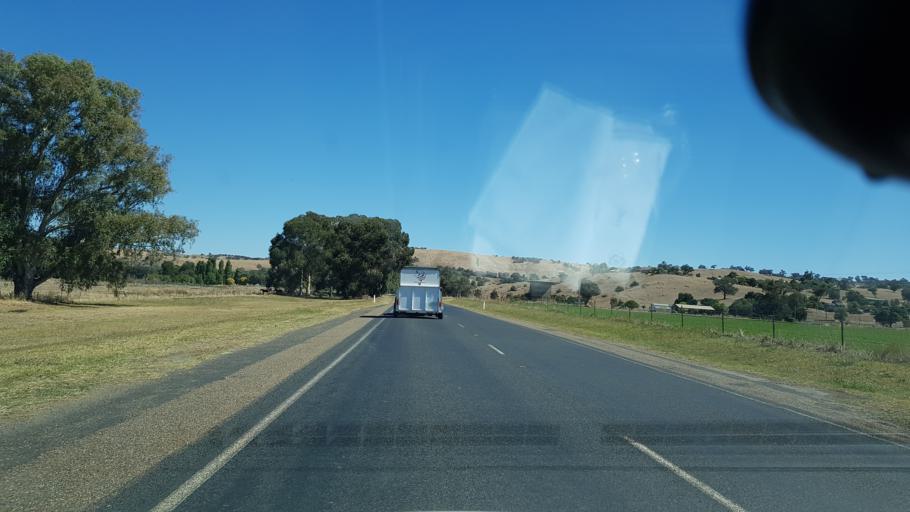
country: AU
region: New South Wales
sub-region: Gundagai
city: Gundagai
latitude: -34.8226
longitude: 148.3385
